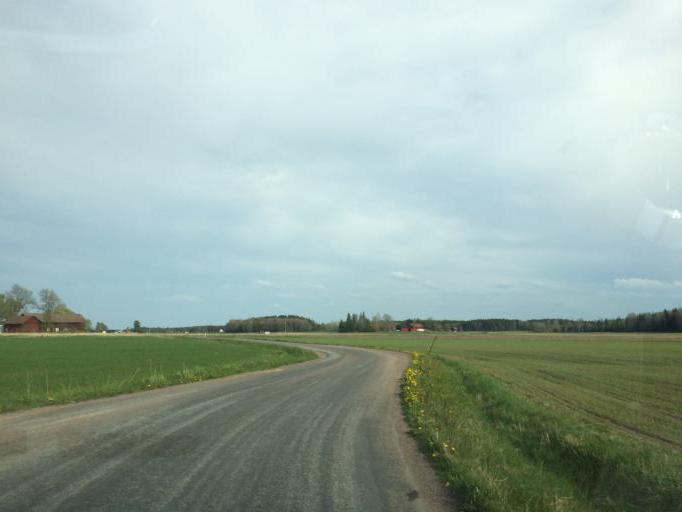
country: SE
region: Vaestmanland
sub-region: Hallstahammars Kommun
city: Hallstahammar
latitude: 59.6017
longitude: 16.1156
